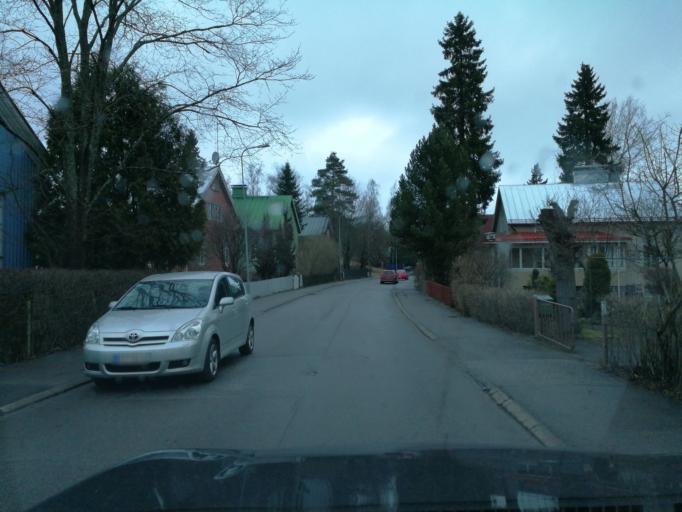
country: FI
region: Uusimaa
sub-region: Helsinki
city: Helsinki
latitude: 60.2088
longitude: 24.9393
